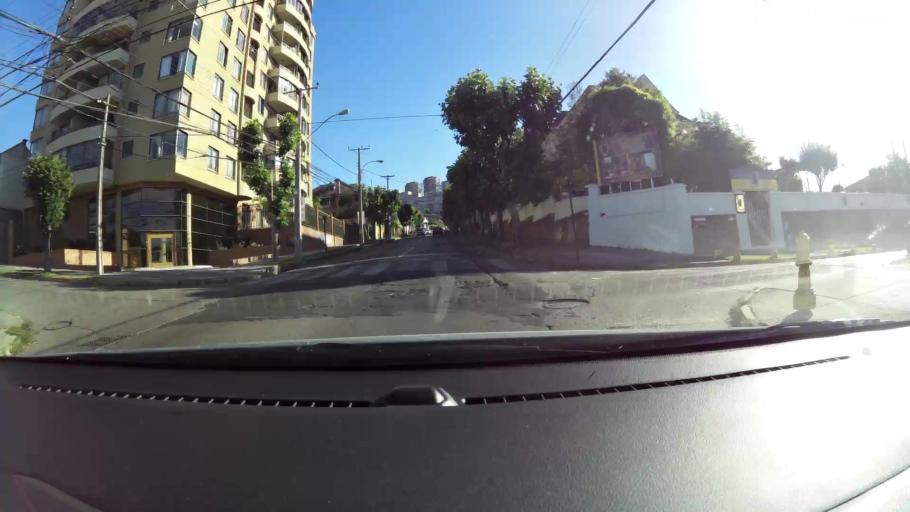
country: CL
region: Valparaiso
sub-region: Provincia de Valparaiso
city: Vina del Mar
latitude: -33.0306
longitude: -71.5640
